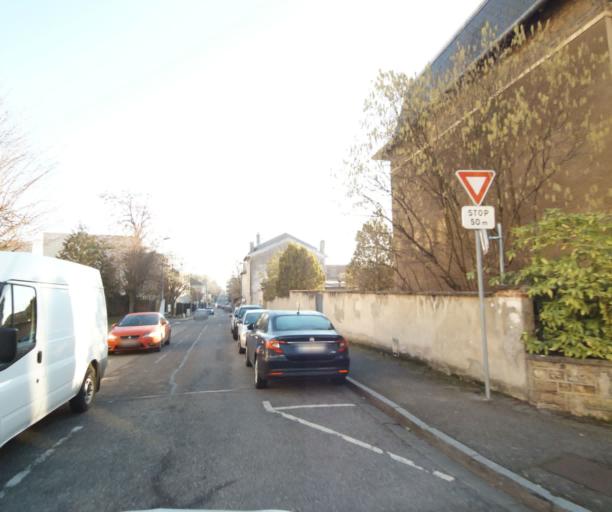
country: FR
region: Lorraine
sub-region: Departement de Meurthe-et-Moselle
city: Laxou
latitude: 48.6868
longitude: 6.1538
